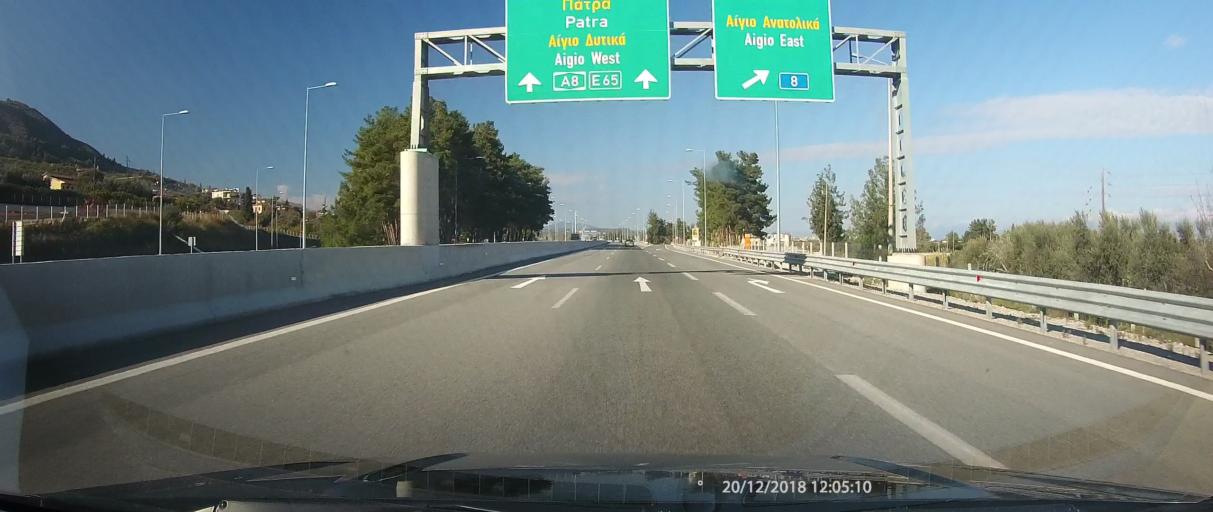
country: GR
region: West Greece
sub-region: Nomos Achaias
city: Temeni
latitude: 38.2196
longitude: 22.1058
